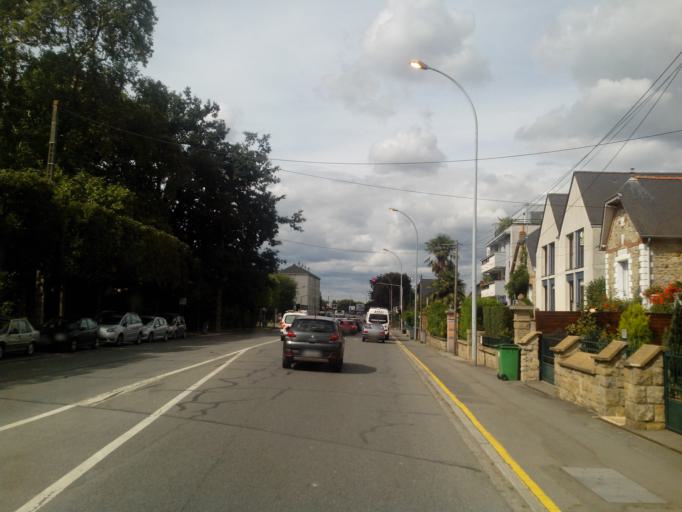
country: FR
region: Brittany
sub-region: Departement d'Ille-et-Vilaine
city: Rennes
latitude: 48.1261
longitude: -1.6858
